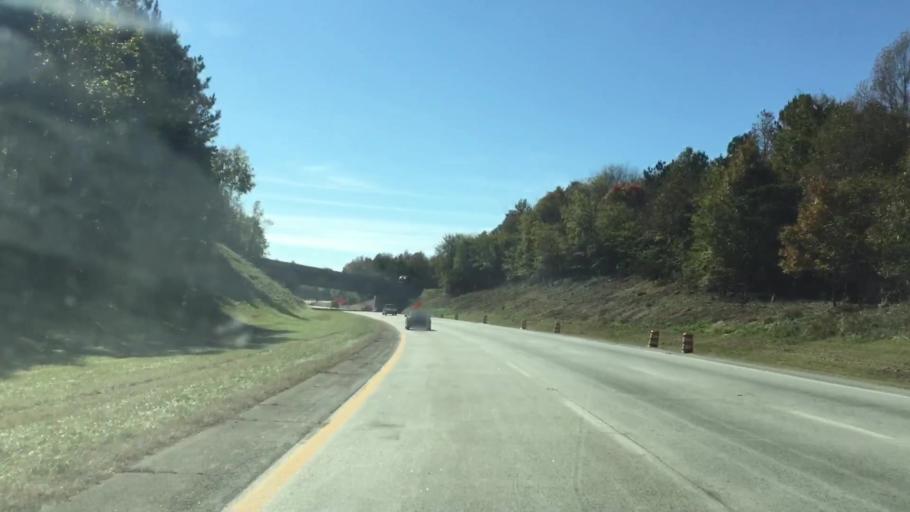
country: US
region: North Carolina
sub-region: Davidson County
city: Thomasville
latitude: 35.8507
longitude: -80.1169
